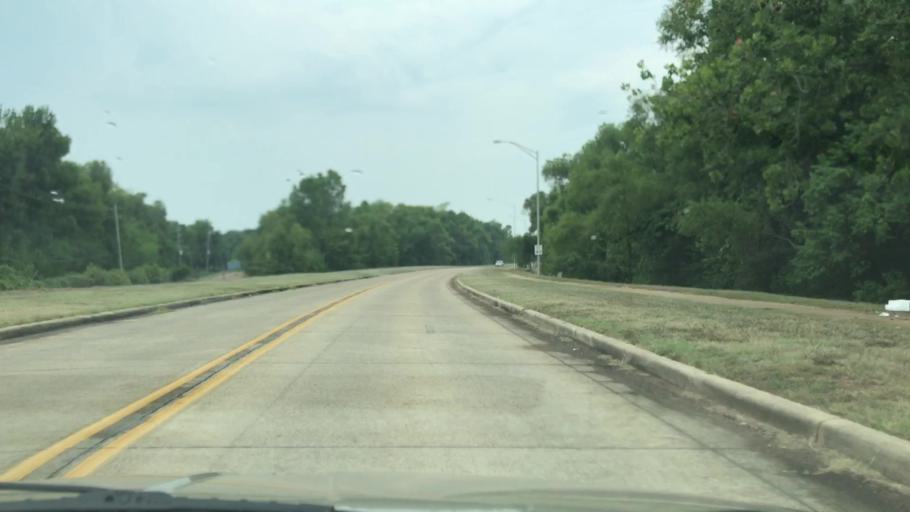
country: US
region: Louisiana
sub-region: Bossier Parish
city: Bossier City
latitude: 32.4721
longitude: -93.6992
